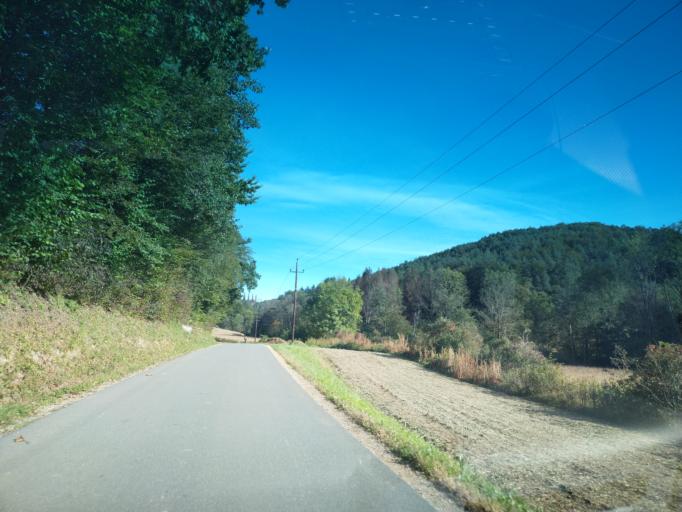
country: AT
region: Styria
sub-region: Politischer Bezirk Leibnitz
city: Sankt Johann im Saggautal
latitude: 46.6984
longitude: 15.4035
